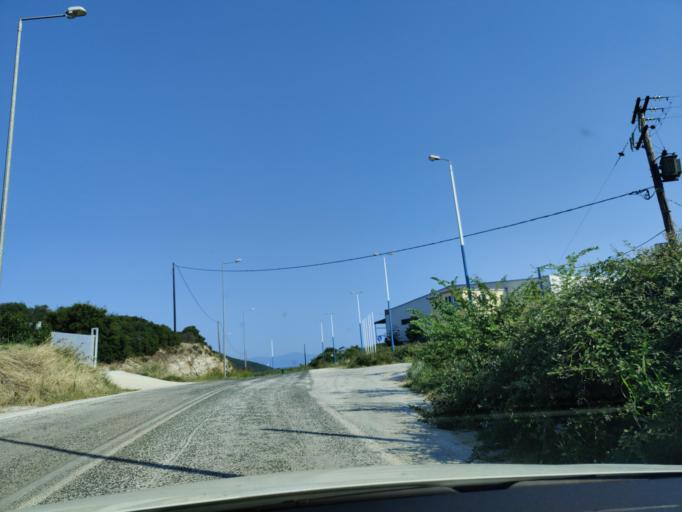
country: GR
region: East Macedonia and Thrace
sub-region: Nomos Kavalas
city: Nea Iraklitsa
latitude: 40.8598
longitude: 24.3042
